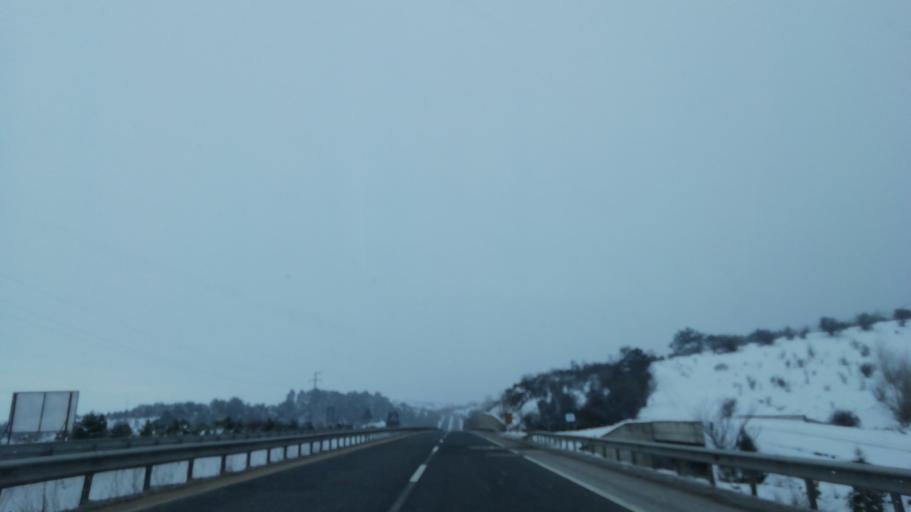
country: TR
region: Bolu
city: Gerede
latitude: 40.8115
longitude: 32.2644
